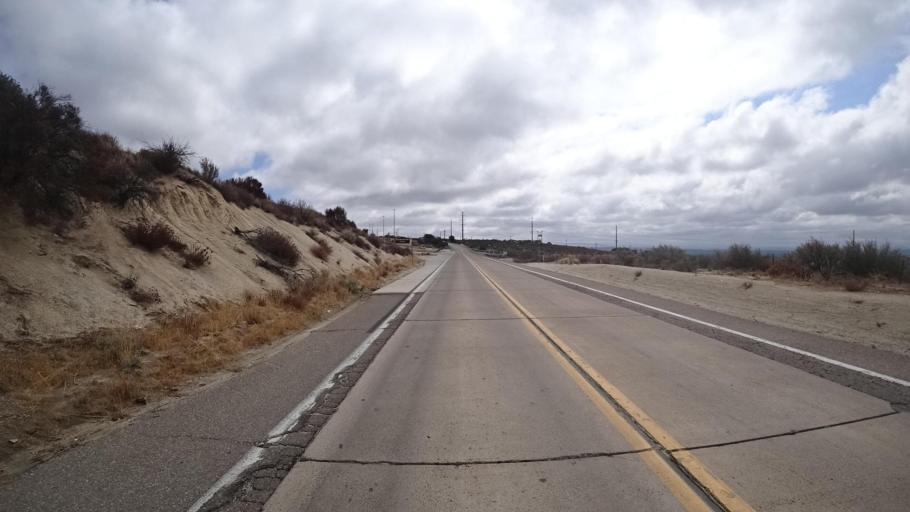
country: US
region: California
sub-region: San Diego County
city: Campo
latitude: 32.7017
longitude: -116.3581
